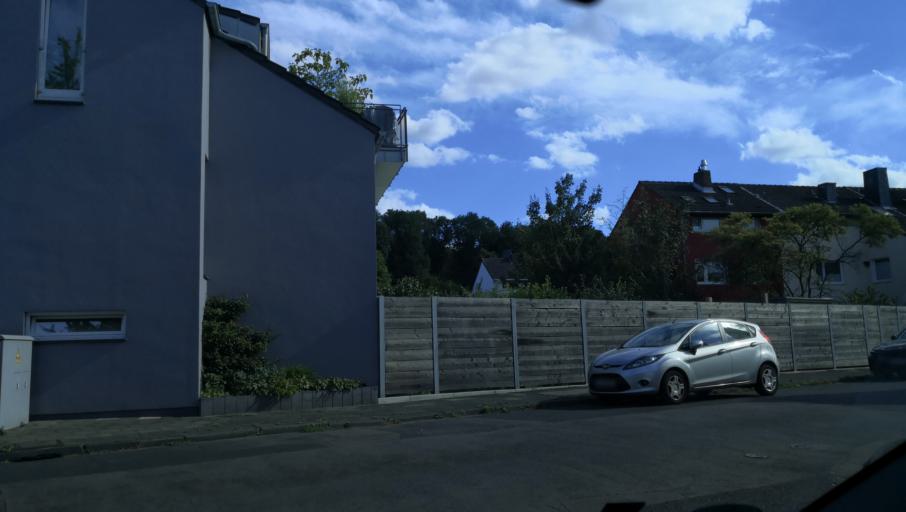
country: DE
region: North Rhine-Westphalia
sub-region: Regierungsbezirk Koln
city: Neustadt/Sued
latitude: 50.9146
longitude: 6.9090
